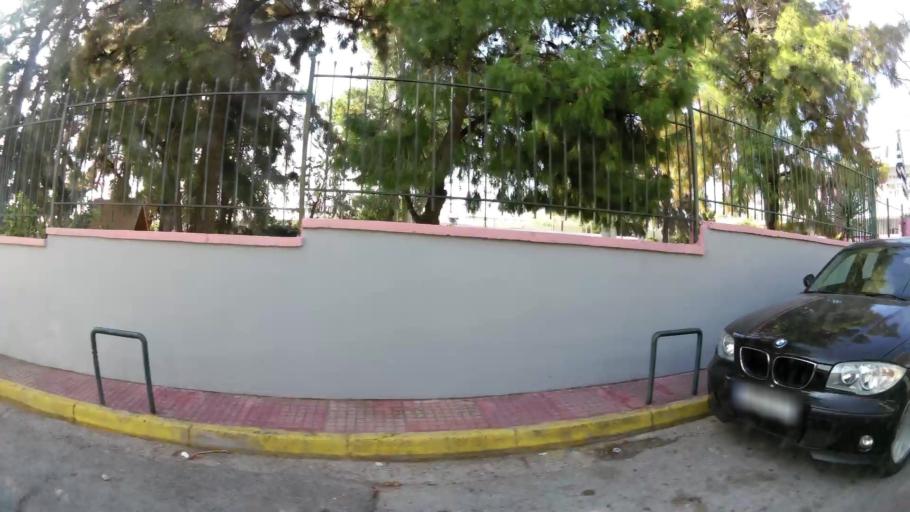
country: GR
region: Attica
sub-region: Nomarchia Athinas
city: Nea Filadelfeia
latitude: 38.0565
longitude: 23.7385
